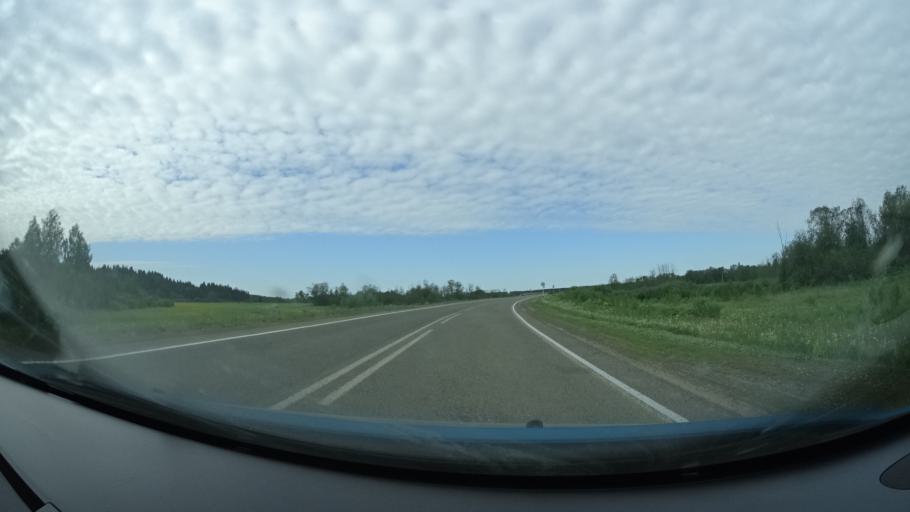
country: RU
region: Perm
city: Kuyeda
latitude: 56.5040
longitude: 55.6250
